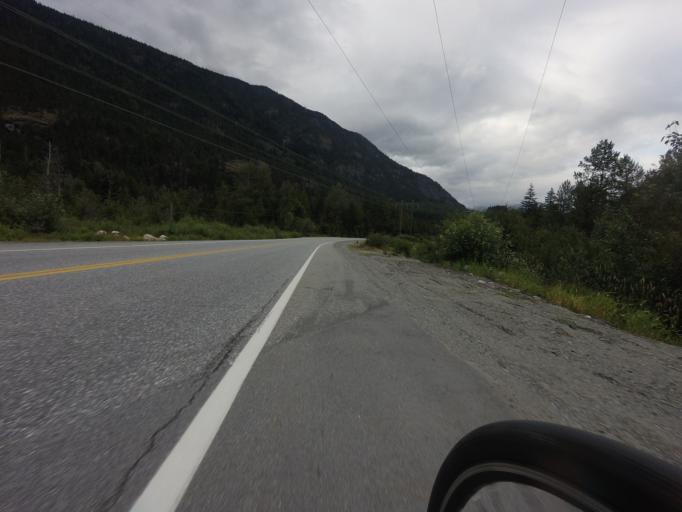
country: CA
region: British Columbia
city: Pemberton
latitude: 50.2804
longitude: -122.8576
